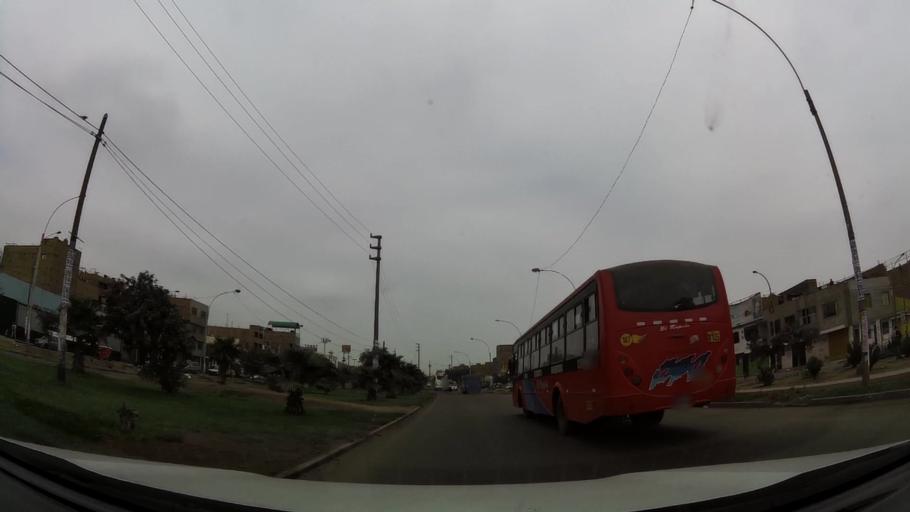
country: PE
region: Lima
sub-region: Lima
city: Independencia
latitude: -12.0087
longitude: -77.0819
